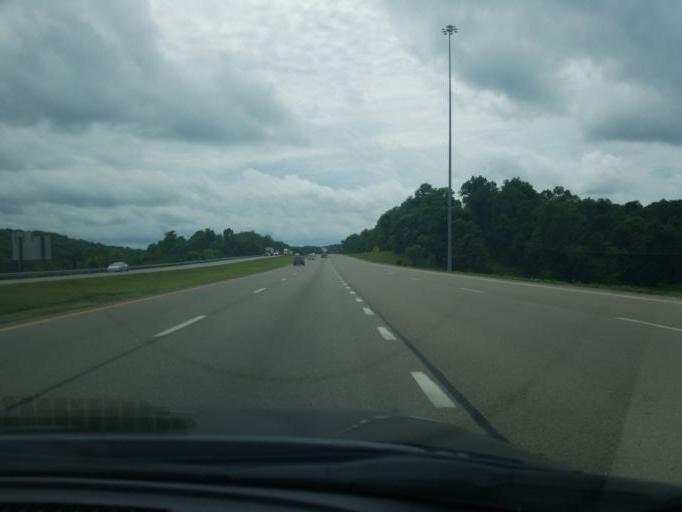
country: US
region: Kentucky
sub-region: Gallatin County
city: Warsaw
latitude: 38.6887
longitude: -84.9457
